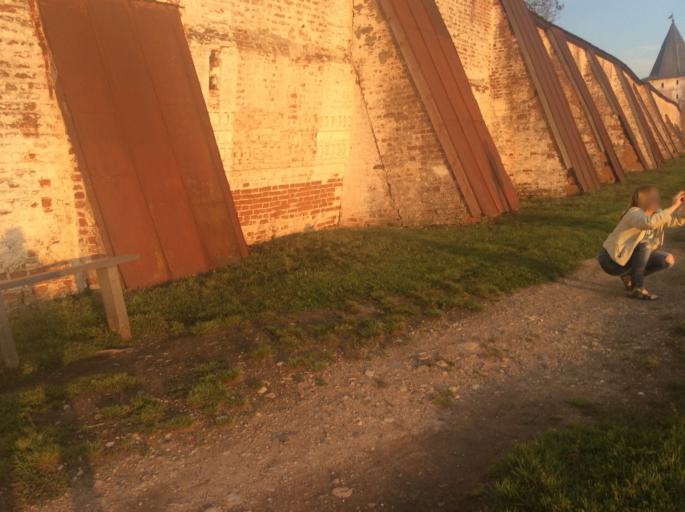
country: RU
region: Vologda
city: Kirillov
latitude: 59.8569
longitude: 38.3655
